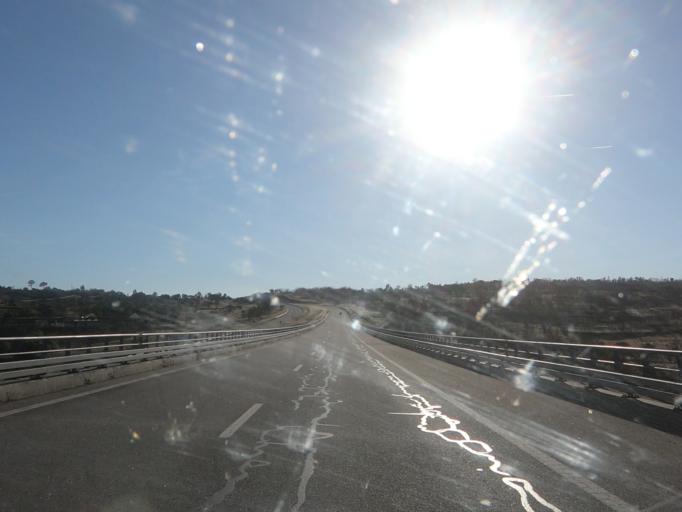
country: PT
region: Guarda
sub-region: Pinhel
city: Pinhel
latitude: 40.6047
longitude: -7.0304
